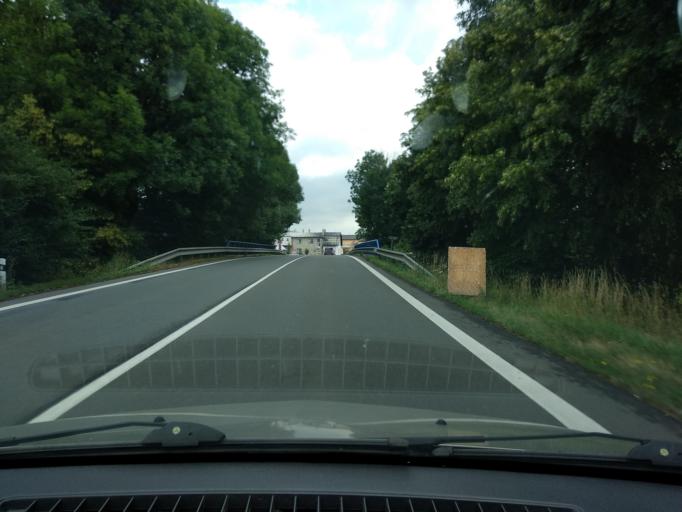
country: CZ
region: Olomoucky
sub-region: Okres Sumperk
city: Bludov
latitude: 49.9265
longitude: 16.9194
